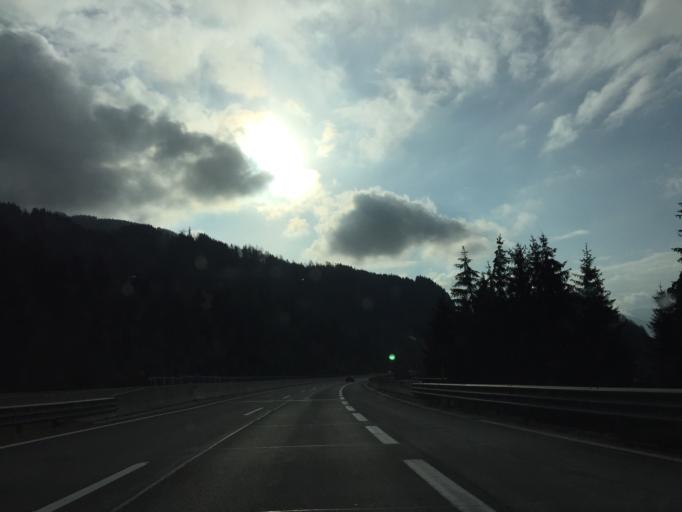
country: AT
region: Salzburg
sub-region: Politischer Bezirk Sankt Johann im Pongau
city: Werfen
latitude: 47.4867
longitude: 13.1906
